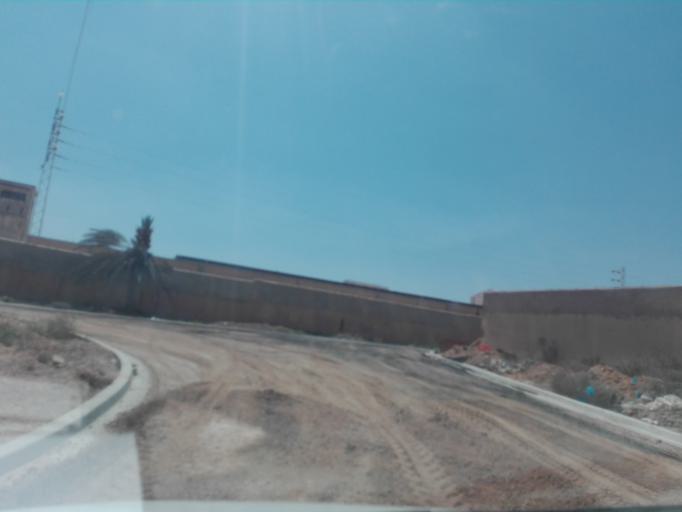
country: TN
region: Safaqis
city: Sfax
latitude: 34.7254
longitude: 10.5172
